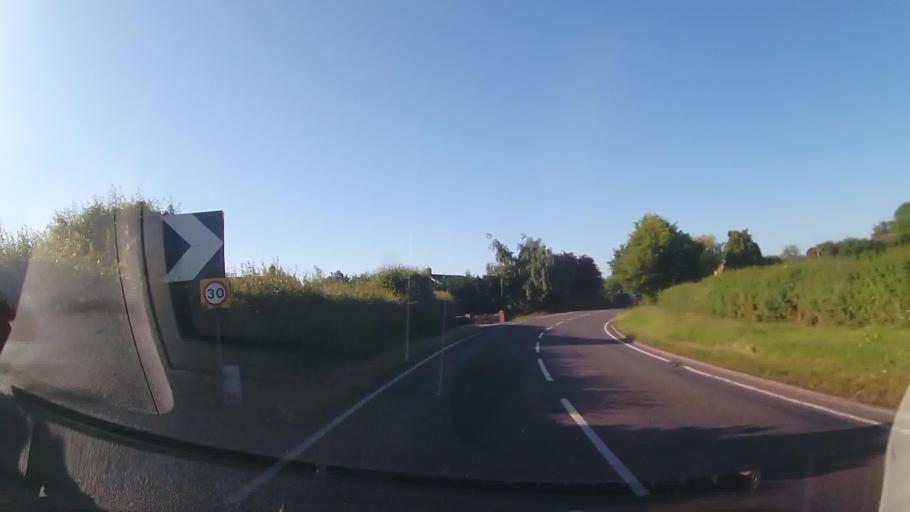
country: GB
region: England
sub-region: Shropshire
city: Withington
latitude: 52.7398
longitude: -2.5728
